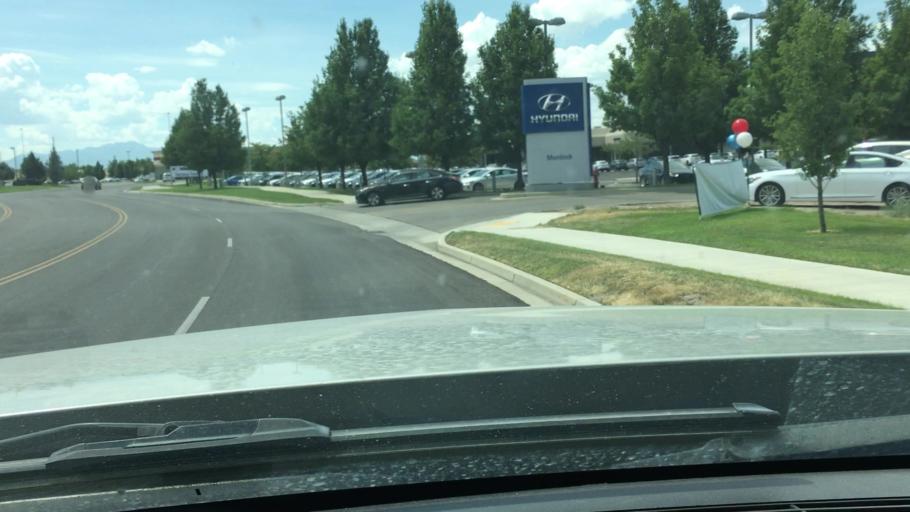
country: US
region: Utah
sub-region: Utah County
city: Lindon
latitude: 40.3298
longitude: -111.7315
